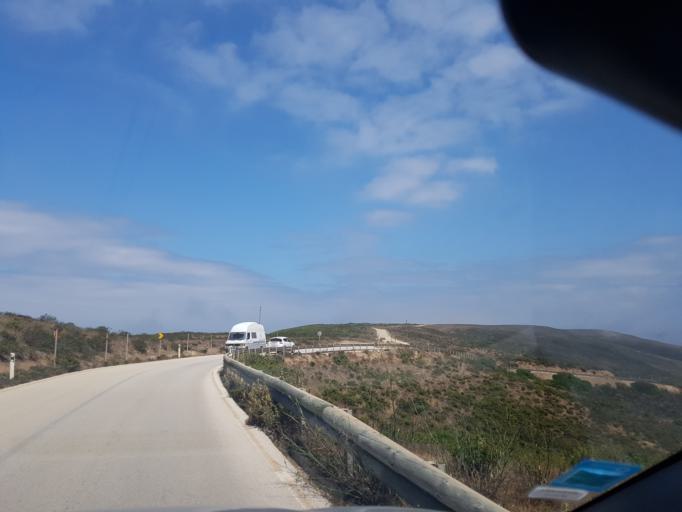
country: PT
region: Faro
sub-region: Vila do Bispo
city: Vila do Bispo
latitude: 37.0969
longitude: -8.9366
